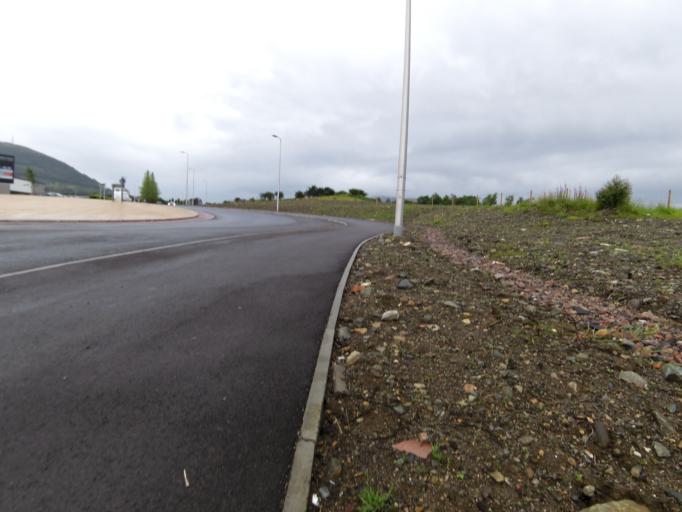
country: GB
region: Scotland
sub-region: Highland
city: Fort William
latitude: 56.8296
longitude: -5.0816
